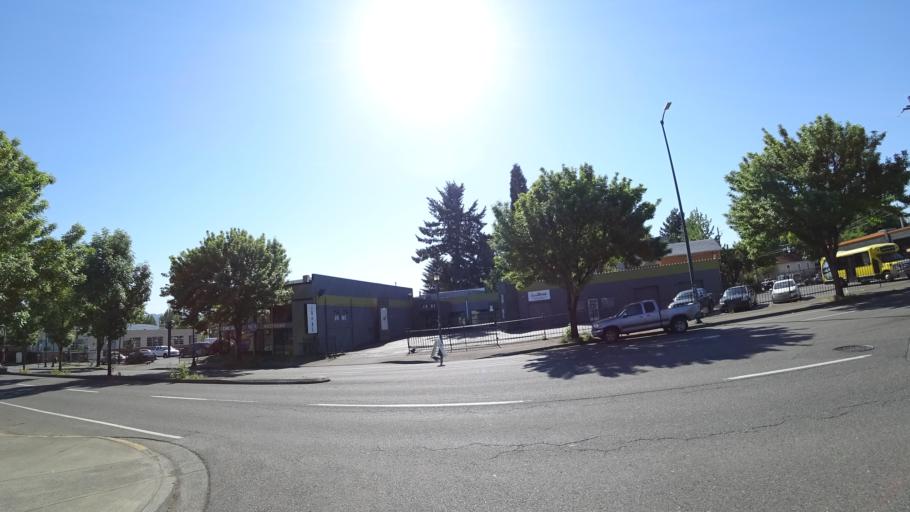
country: US
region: Oregon
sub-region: Multnomah County
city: Portland
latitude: 45.5387
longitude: -122.6615
